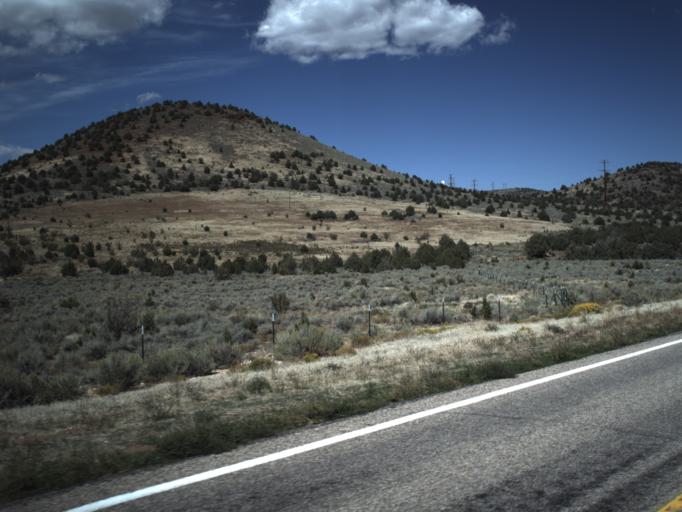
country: US
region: Utah
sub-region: Washington County
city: Enterprise
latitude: 37.3974
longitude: -113.6429
